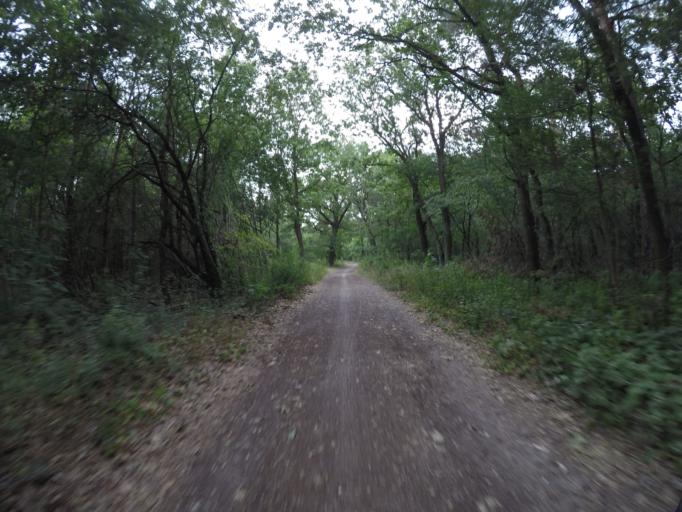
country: DE
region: Berlin
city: Baumschulenweg
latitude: 52.4520
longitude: 13.4906
